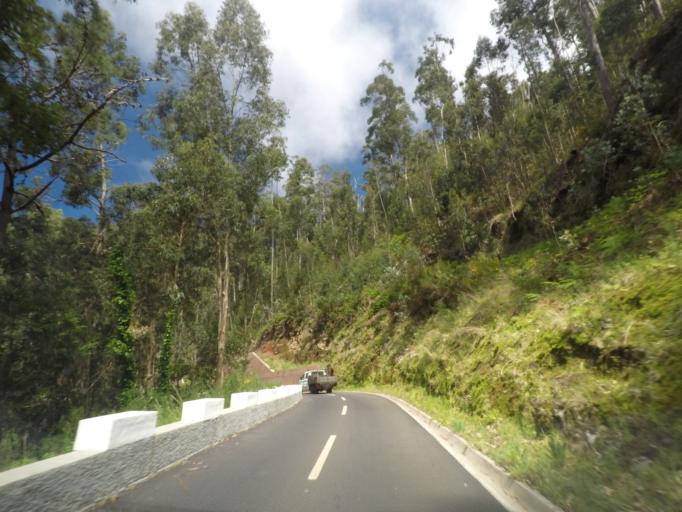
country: PT
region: Madeira
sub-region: Calheta
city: Arco da Calheta
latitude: 32.7277
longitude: -17.1205
